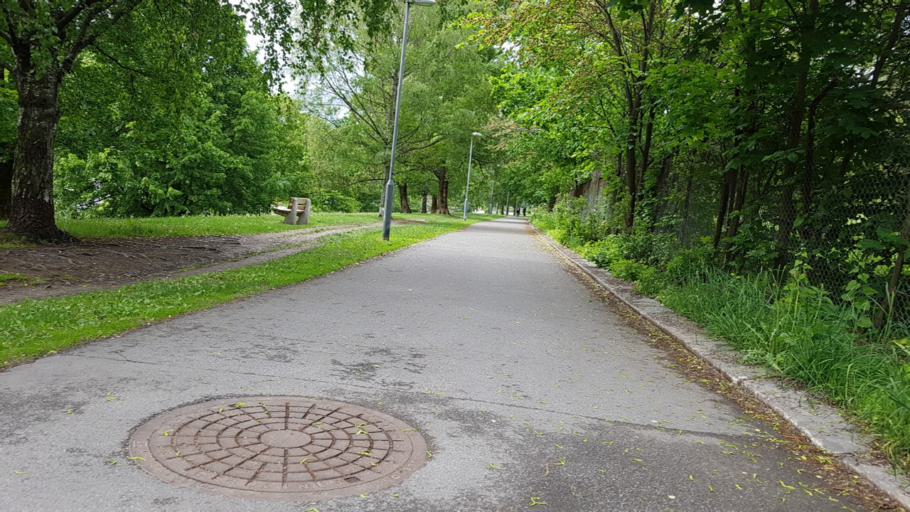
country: NO
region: Oslo
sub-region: Oslo
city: Oslo
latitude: 59.9333
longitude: 10.7744
